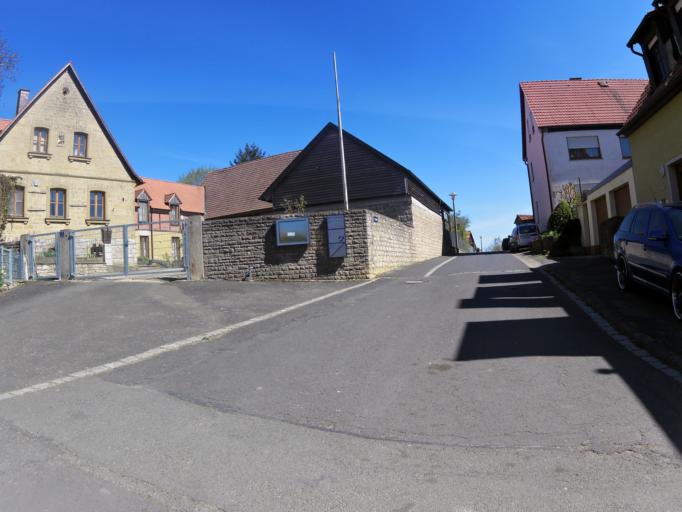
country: DE
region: Bavaria
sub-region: Regierungsbezirk Unterfranken
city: Biebelried
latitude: 49.7973
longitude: 10.0829
